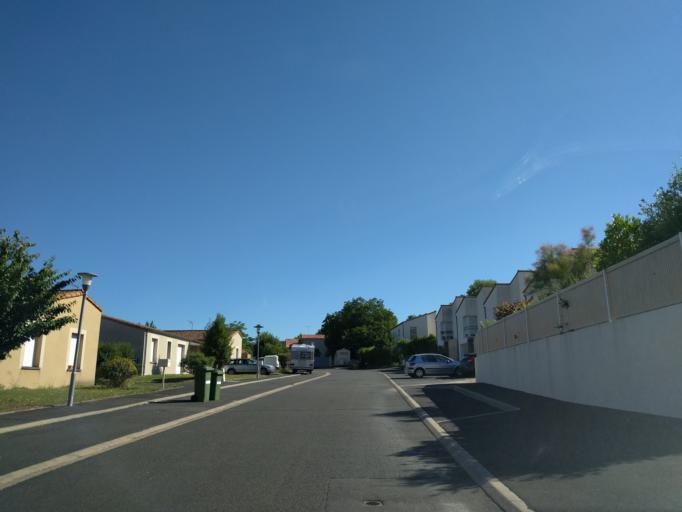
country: FR
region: Poitou-Charentes
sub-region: Departement des Deux-Sevres
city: Niort
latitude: 46.3410
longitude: -0.4478
